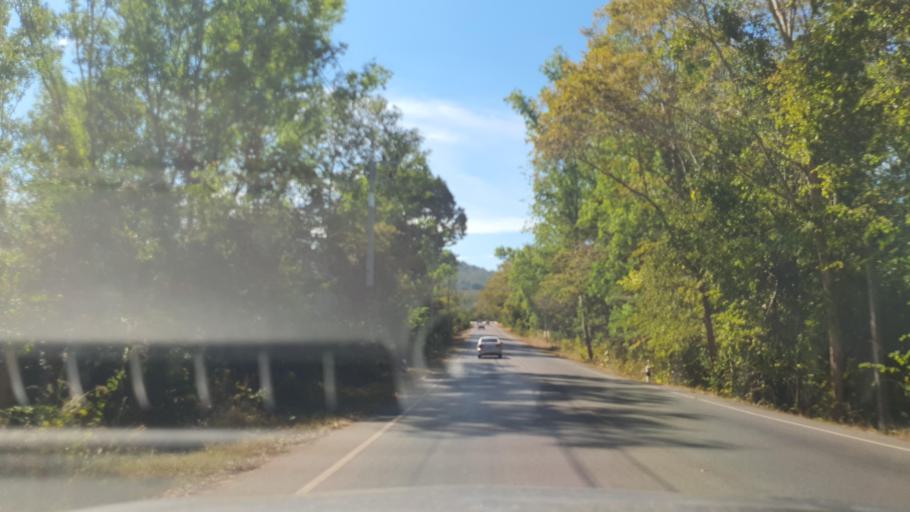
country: TH
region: Kalasin
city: Khao Wong
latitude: 16.7654
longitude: 104.1362
